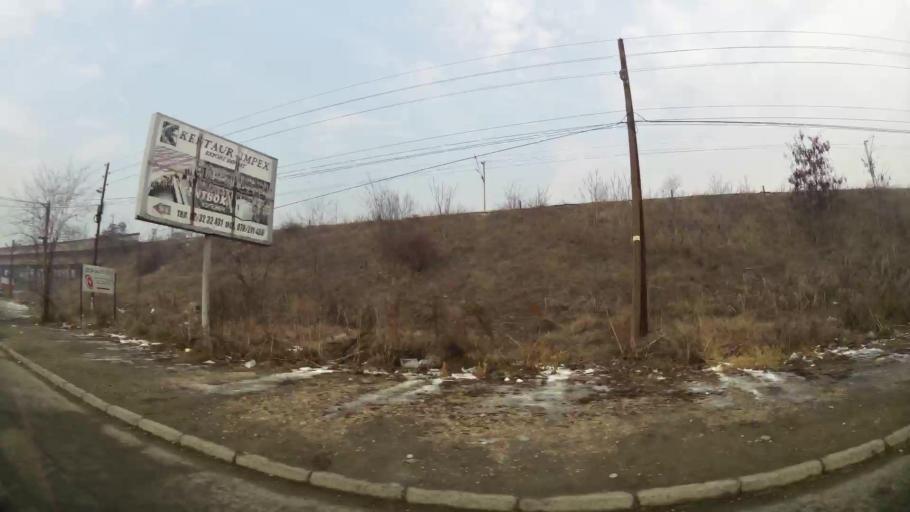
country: MK
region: Karpos
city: Skopje
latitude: 41.9963
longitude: 21.4541
